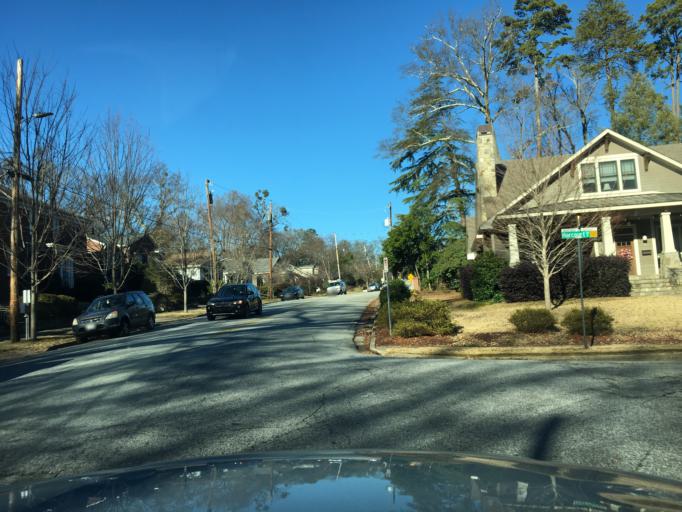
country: US
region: South Carolina
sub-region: Greenville County
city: Greenville
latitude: 34.8586
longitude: -82.3903
